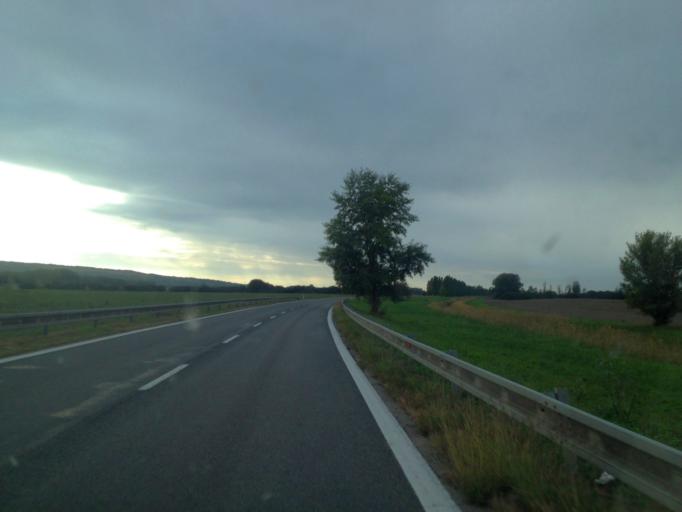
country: HU
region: Komarom-Esztergom
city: Labatlan
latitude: 47.7612
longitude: 18.5192
